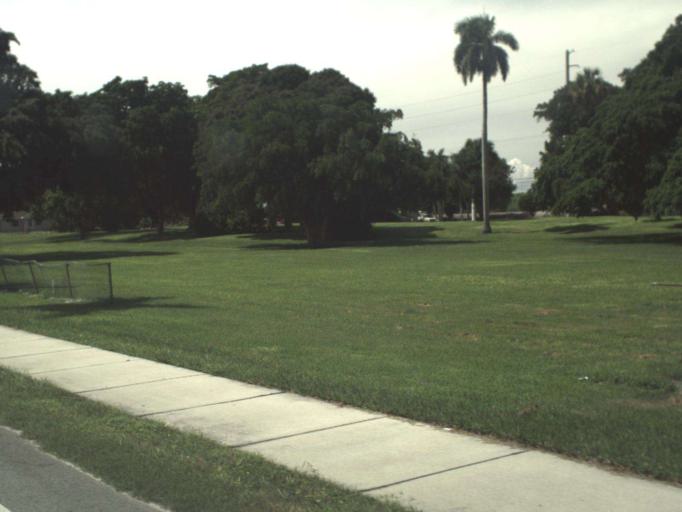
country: US
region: Florida
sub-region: Palm Beach County
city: Pahokee
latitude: 26.8614
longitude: -80.6316
